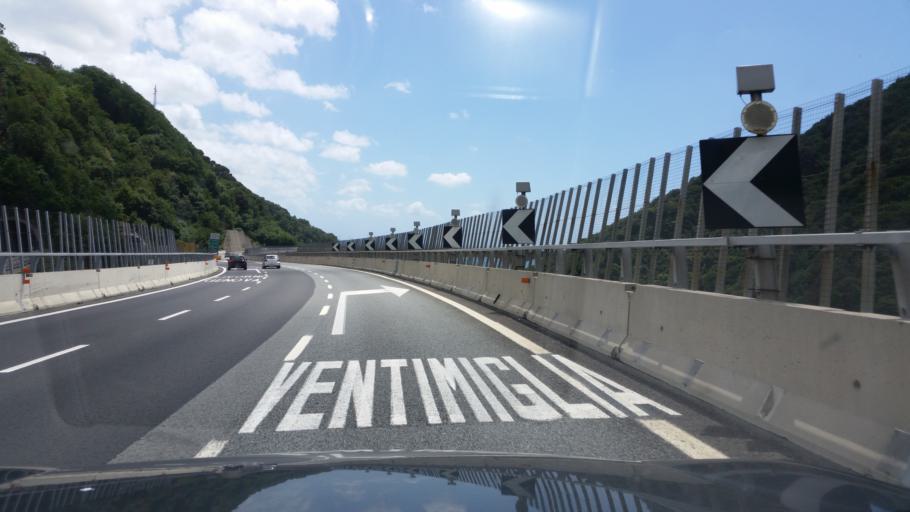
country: IT
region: Liguria
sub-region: Provincia di Genova
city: Mele
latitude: 44.4350
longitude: 8.7382
